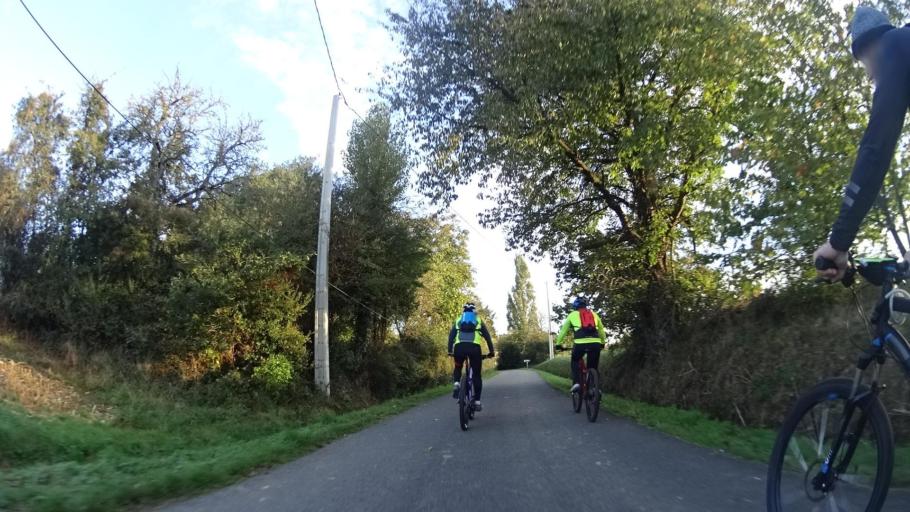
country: FR
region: Brittany
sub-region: Departement des Cotes-d'Armor
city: Evran
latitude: 48.3488
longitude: -1.9406
